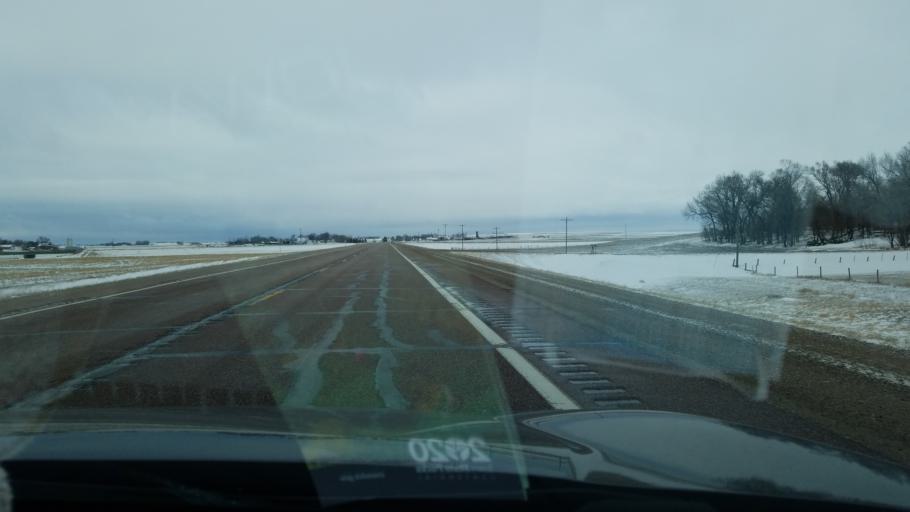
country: US
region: Iowa
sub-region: Plymouth County
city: Le Mars
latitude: 42.9206
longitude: -96.1750
